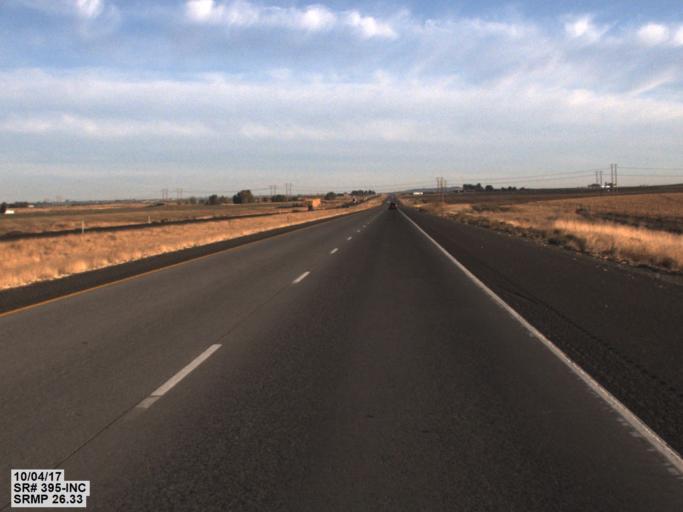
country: US
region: Washington
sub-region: Franklin County
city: Pasco
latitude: 46.3028
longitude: -119.0932
